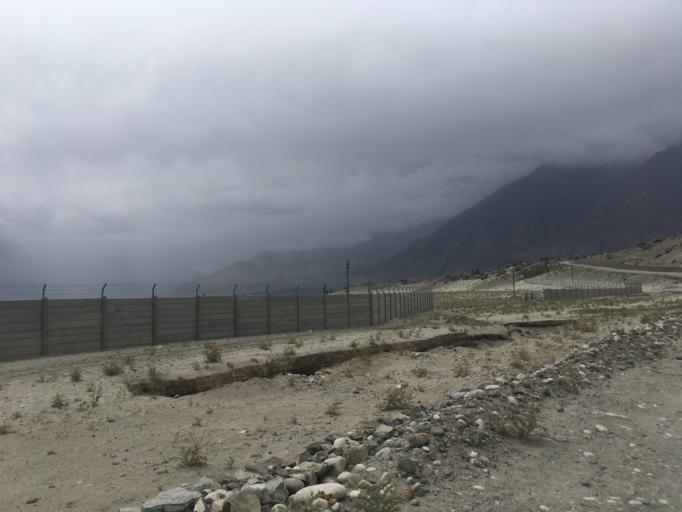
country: PK
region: Gilgit-Baltistan
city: Skardu
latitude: 35.3159
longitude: 75.6574
